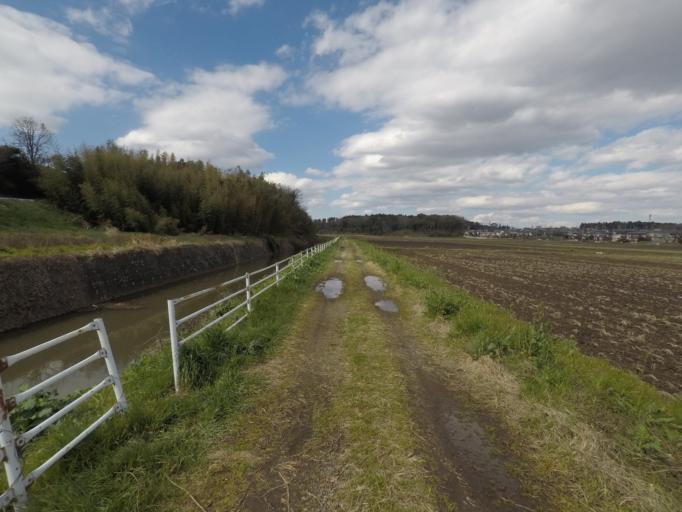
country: JP
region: Ibaraki
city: Ushiku
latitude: 35.9880
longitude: 140.1195
